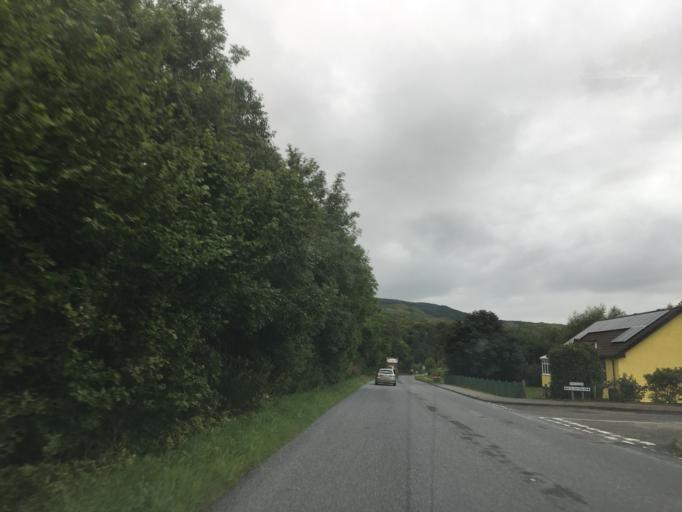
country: GB
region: Scotland
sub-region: Argyll and Bute
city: Oban
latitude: 56.2584
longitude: -5.4765
